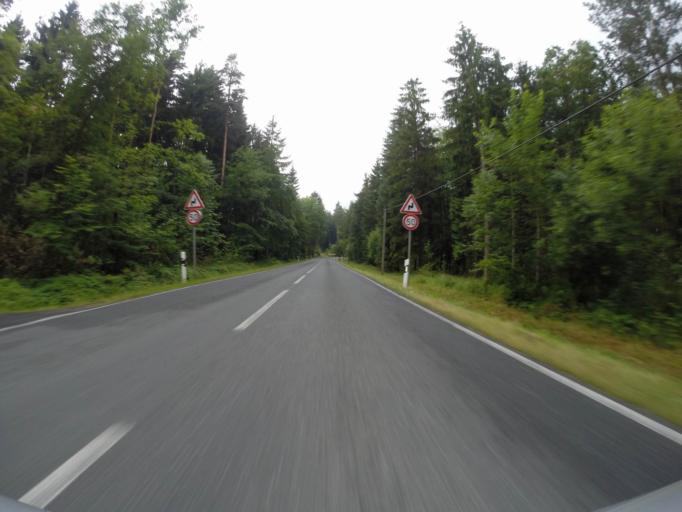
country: DE
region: Thuringia
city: Albersdorf
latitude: 50.8948
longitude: 11.7650
